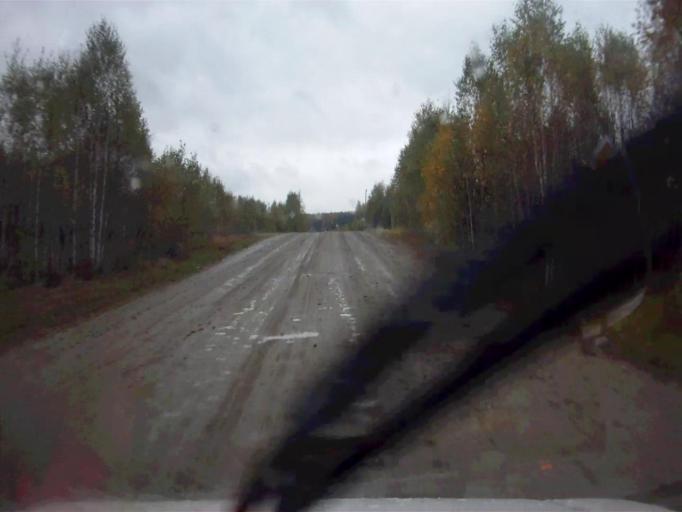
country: RU
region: Chelyabinsk
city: Kyshtym
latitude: 55.8471
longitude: 60.4852
